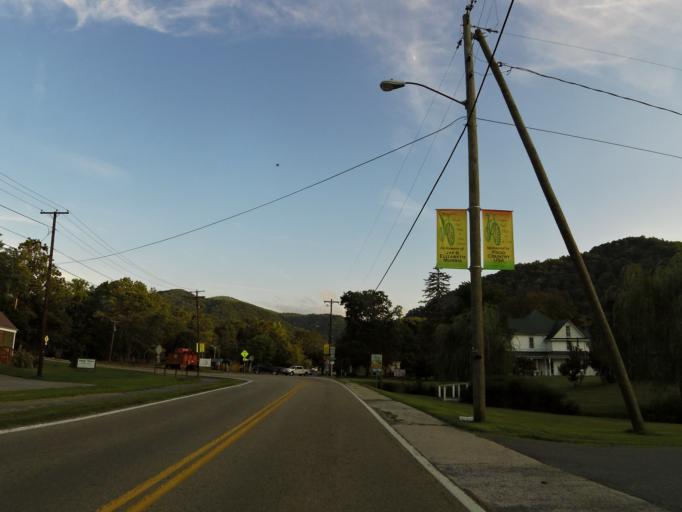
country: US
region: Virginia
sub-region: Washington County
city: Emory
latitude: 36.6365
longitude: -81.7924
